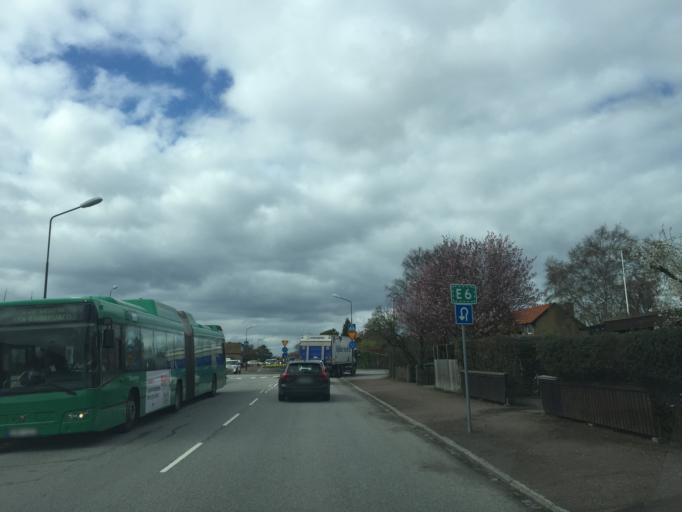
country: SE
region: Skane
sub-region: Malmo
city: Malmoe
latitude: 55.5782
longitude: 12.9651
